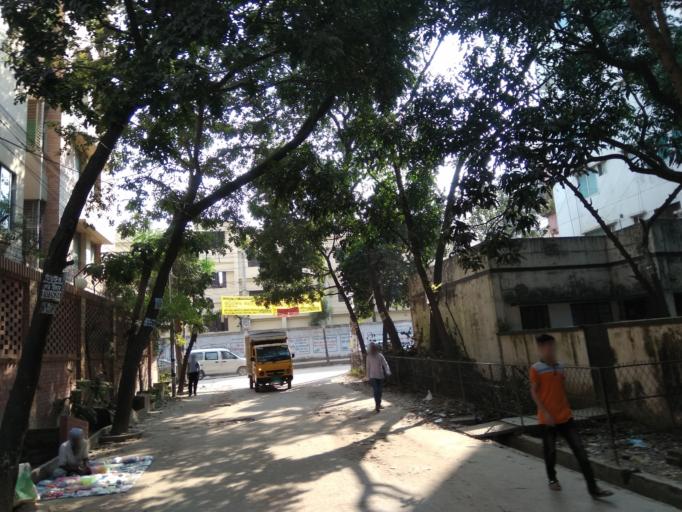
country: BD
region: Dhaka
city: Tungi
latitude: 23.8266
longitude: 90.3616
